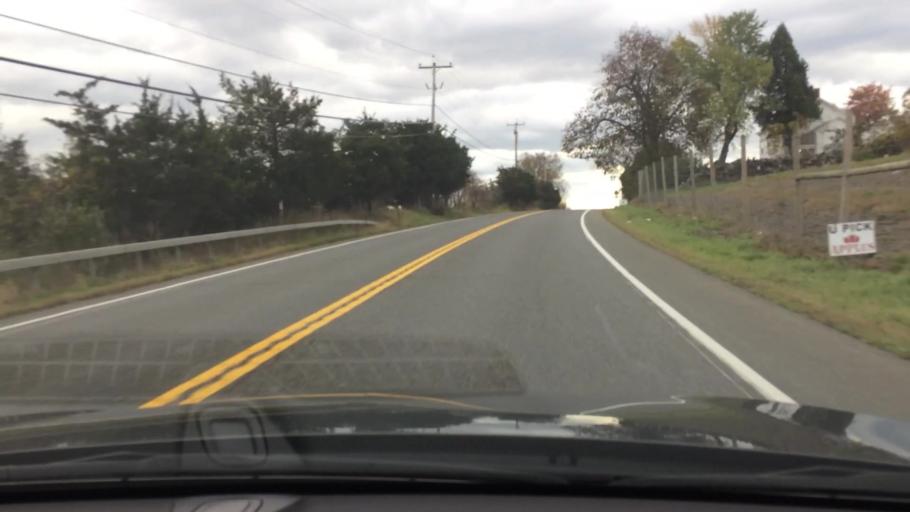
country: US
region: New York
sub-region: Columbia County
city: Stottville
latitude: 42.3133
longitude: -73.7014
